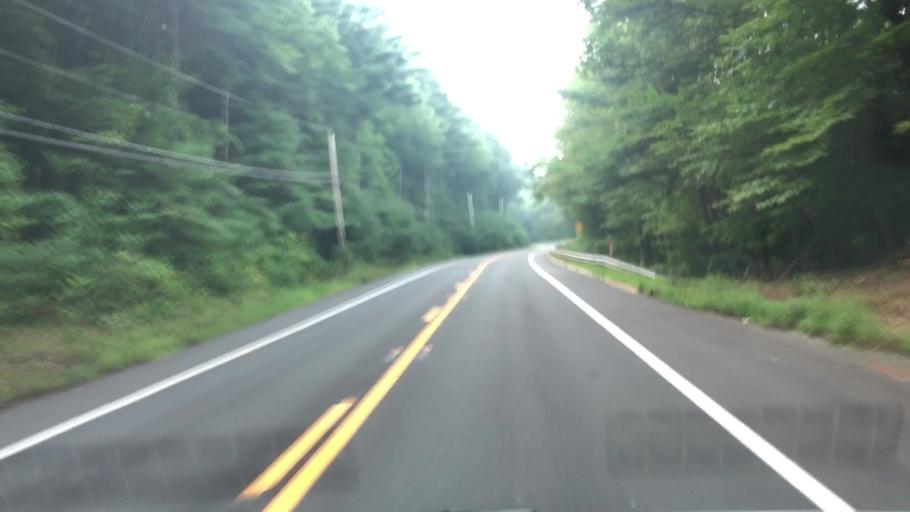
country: US
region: Massachusetts
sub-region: Franklin County
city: Ashfield
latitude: 42.5477
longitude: -72.8015
